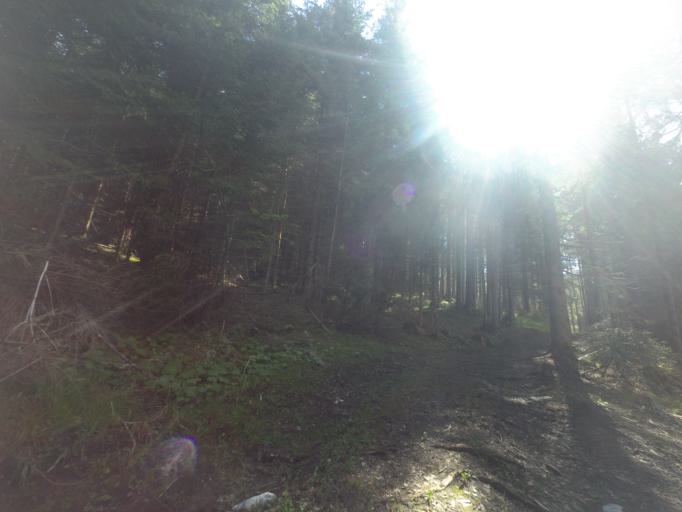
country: AT
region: Salzburg
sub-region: Politischer Bezirk Zell am See
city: Lend
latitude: 47.3083
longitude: 13.0566
